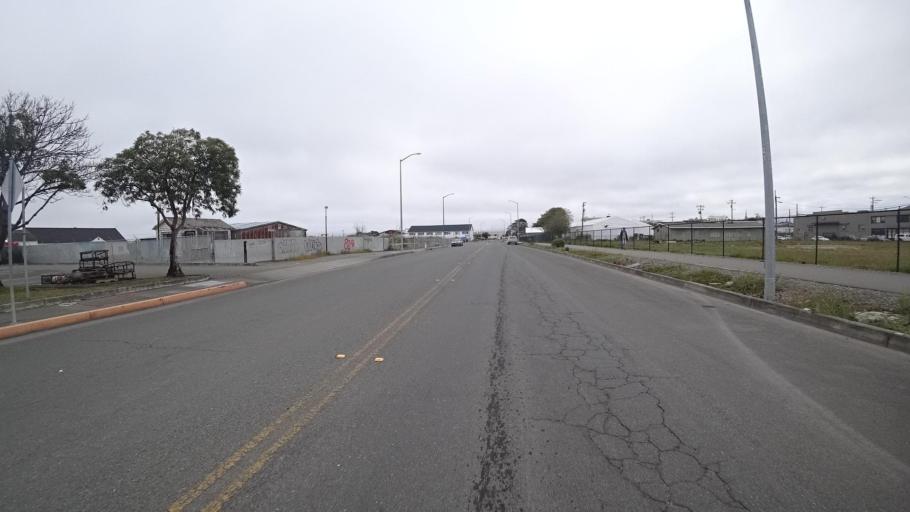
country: US
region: California
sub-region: Humboldt County
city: Eureka
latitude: 40.8042
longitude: -124.1735
